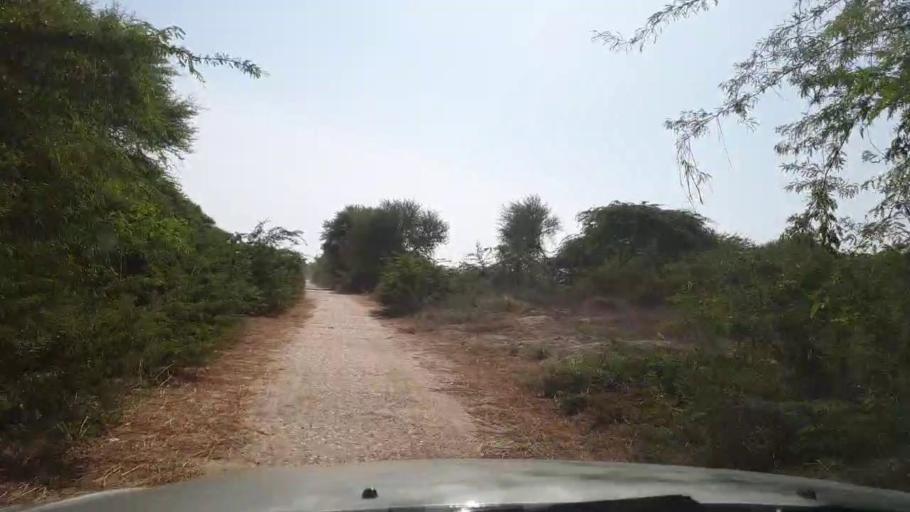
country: PK
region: Sindh
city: Bulri
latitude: 24.9569
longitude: 68.3259
